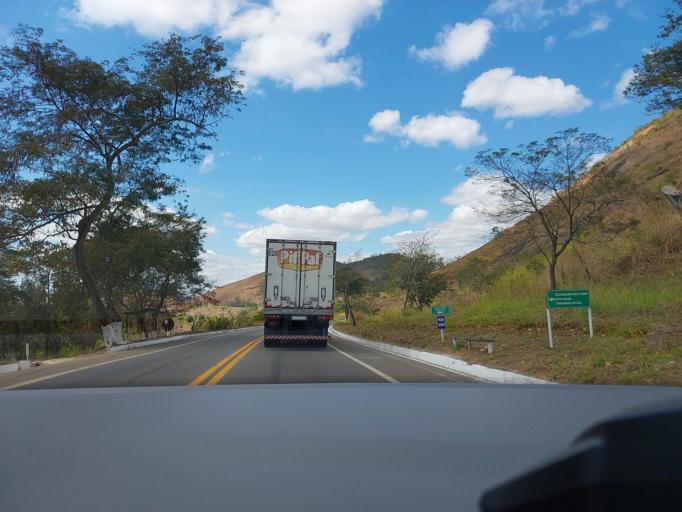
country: BR
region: Minas Gerais
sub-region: Muriae
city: Muriae
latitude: -21.1263
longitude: -42.2488
